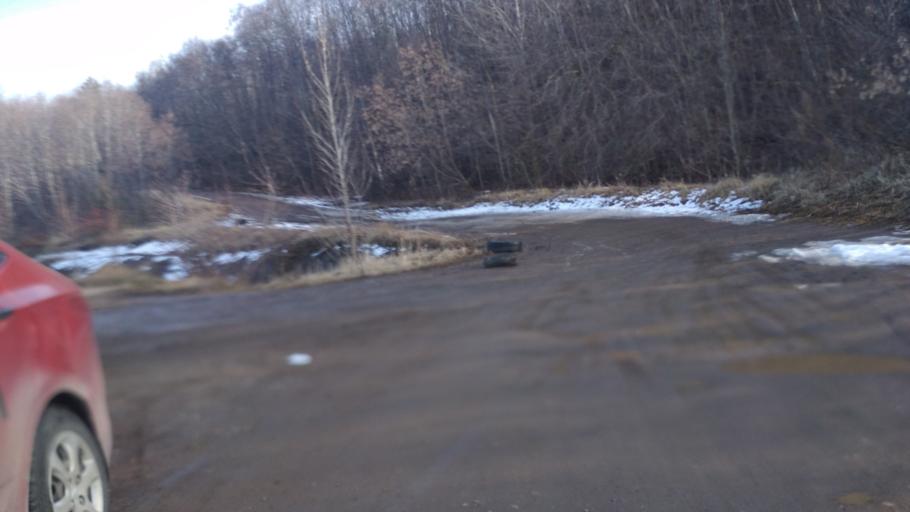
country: RU
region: Chuvashia
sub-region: Cheboksarskiy Rayon
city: Cheboksary
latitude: 56.1443
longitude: 47.3250
